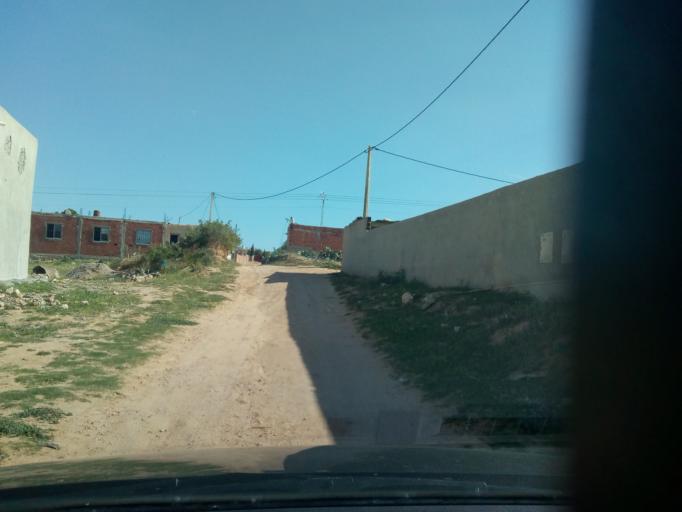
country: TN
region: Safaqis
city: Sfax
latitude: 34.7312
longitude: 10.5992
